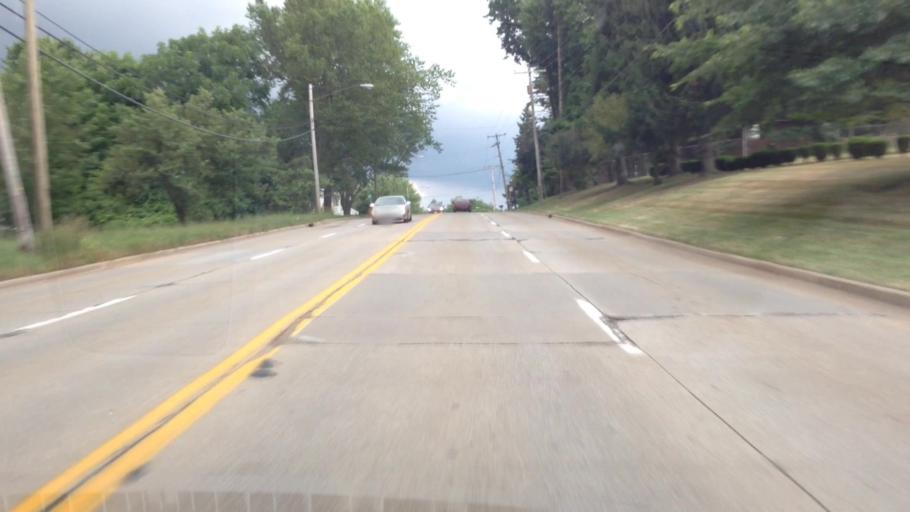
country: US
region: Ohio
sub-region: Summit County
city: Barberton
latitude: 41.0419
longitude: -81.5816
